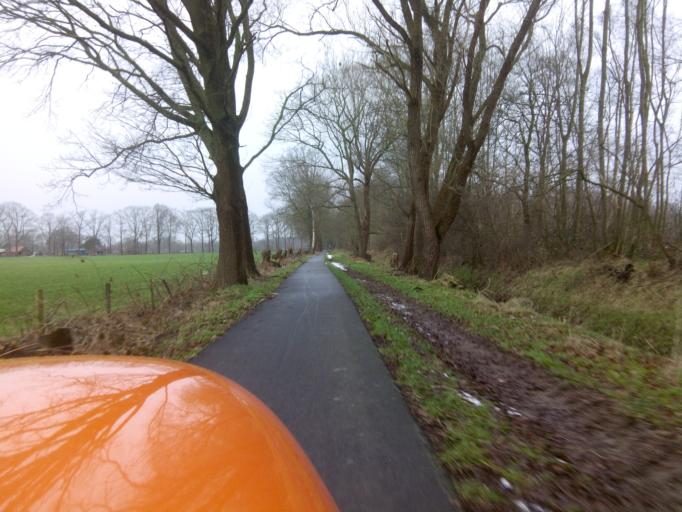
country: NL
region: Gelderland
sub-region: Gemeente Nijkerk
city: Nijkerk
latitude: 52.2198
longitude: 5.5319
